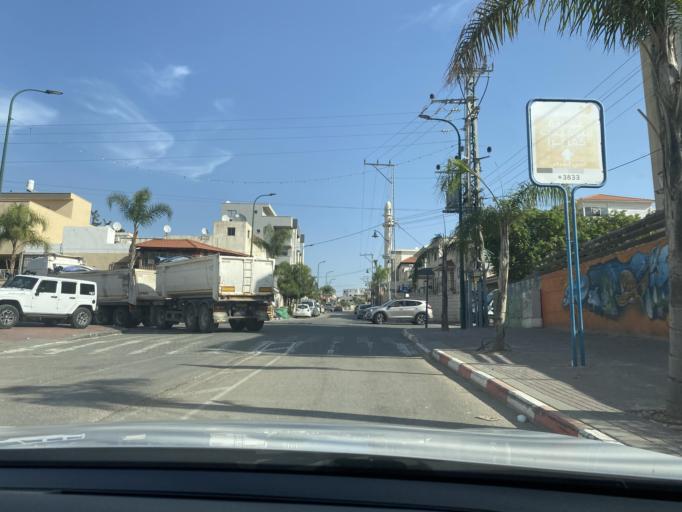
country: IL
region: Central District
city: Kafr Qasim
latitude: 32.1314
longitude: 34.9673
